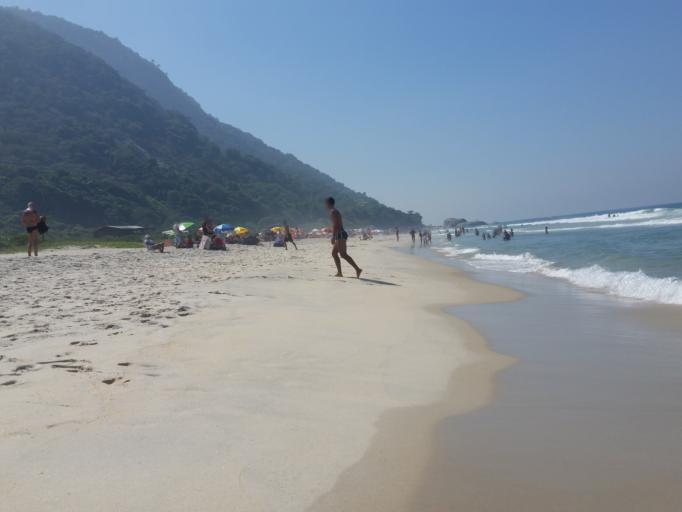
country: BR
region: Rio de Janeiro
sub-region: Nilopolis
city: Nilopolis
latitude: -23.0483
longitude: -43.5205
